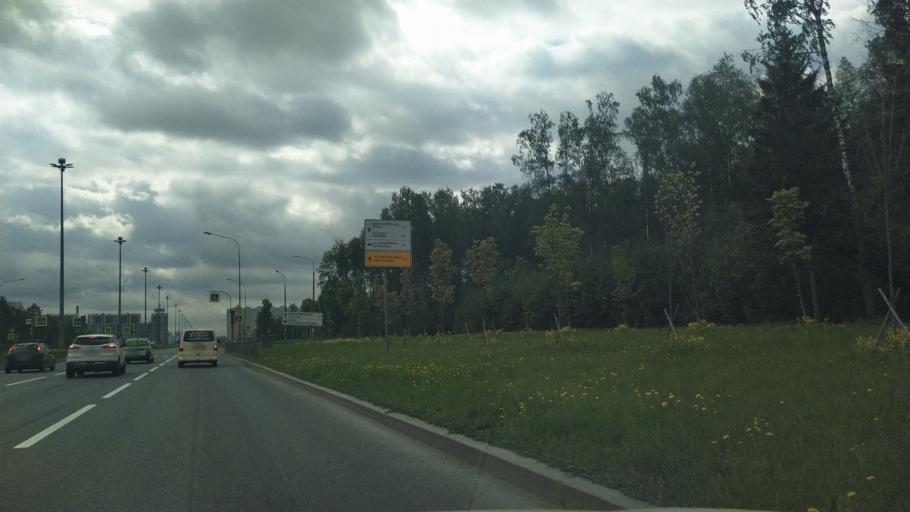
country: RU
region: Leningrad
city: Untolovo
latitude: 60.0488
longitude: 30.2313
